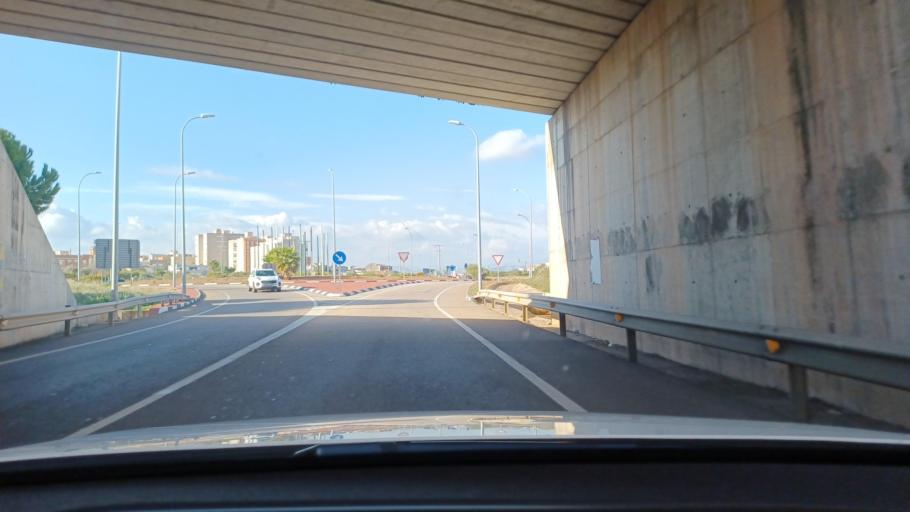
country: ES
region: Valencia
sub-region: Provincia de Castello
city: Betxi
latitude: 39.9265
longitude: -0.1910
